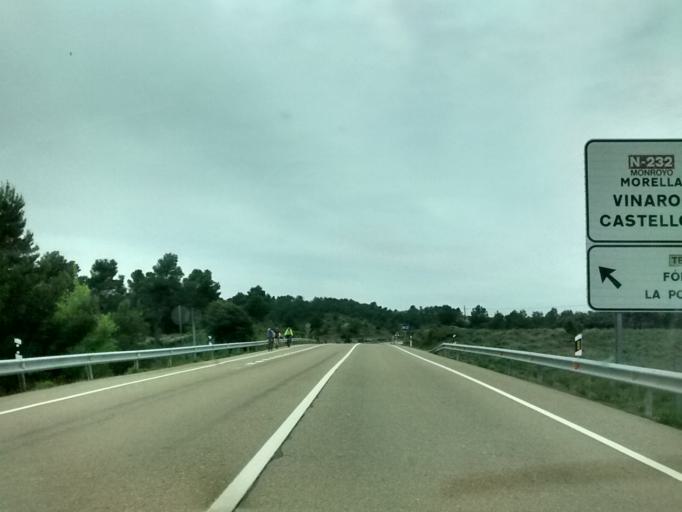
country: ES
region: Aragon
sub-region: Provincia de Teruel
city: Fornoles
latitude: 40.9179
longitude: -0.0189
